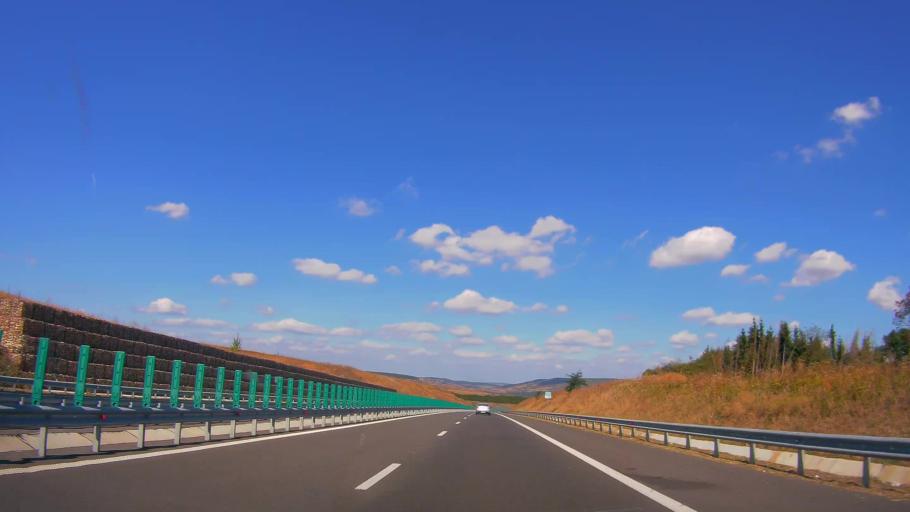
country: RO
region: Cluj
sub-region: Comuna Baciu
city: Mera
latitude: 46.7869
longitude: 23.4161
